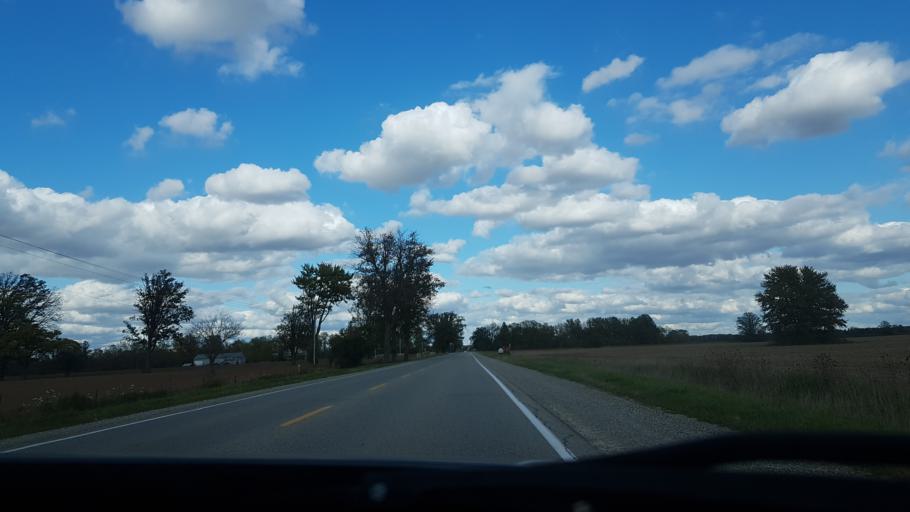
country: CA
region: Ontario
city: South Huron
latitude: 43.0966
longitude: -81.5688
